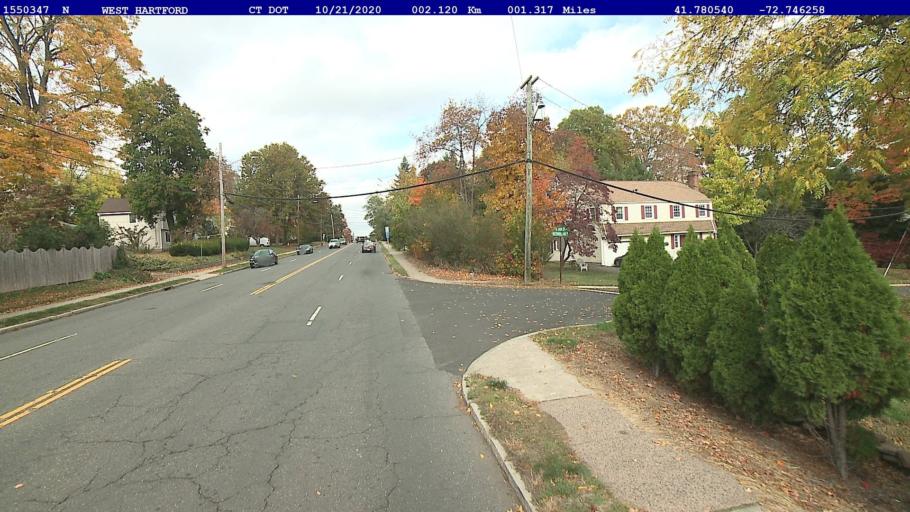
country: US
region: Connecticut
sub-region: Hartford County
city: West Hartford
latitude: 41.7805
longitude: -72.7463
